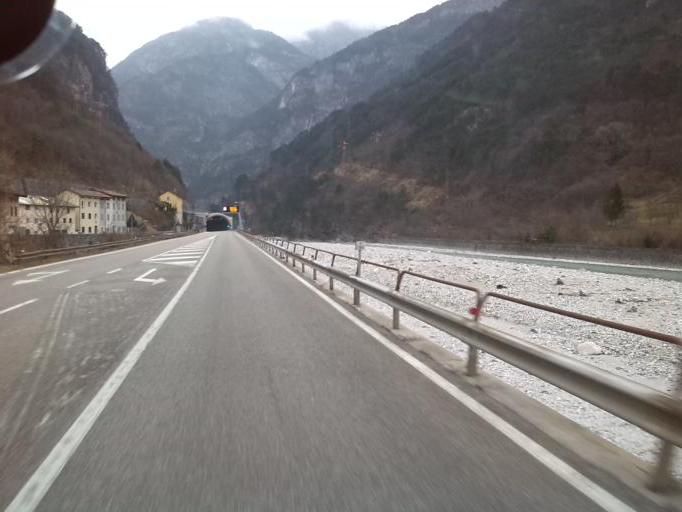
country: IT
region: Friuli Venezia Giulia
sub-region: Provincia di Udine
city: Chiusaforte
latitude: 46.4091
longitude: 13.3120
